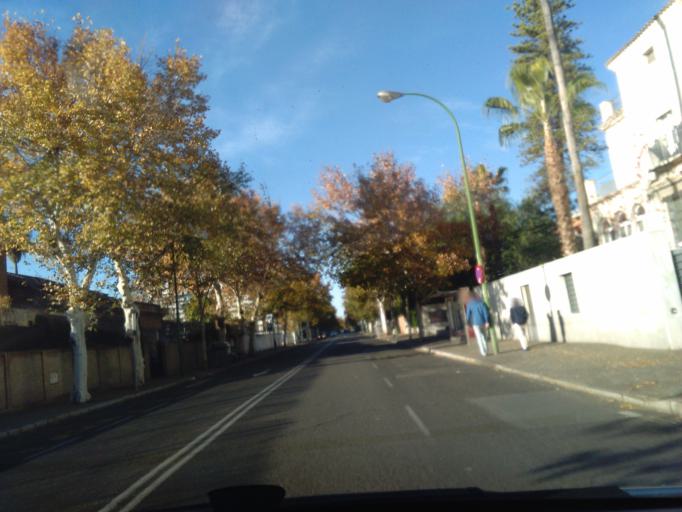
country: ES
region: Andalusia
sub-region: Provincia de Sevilla
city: Sevilla
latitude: 37.3592
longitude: -5.9804
